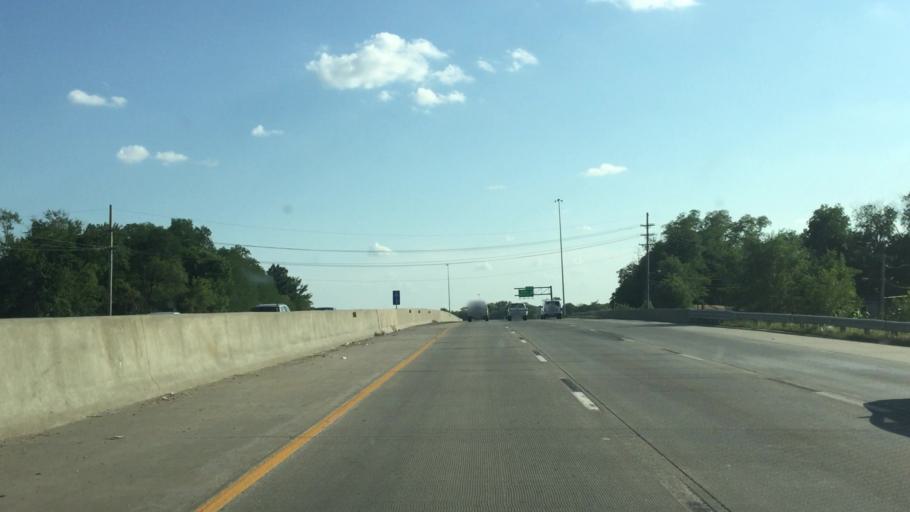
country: US
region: Kansas
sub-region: Wyandotte County
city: Kansas City
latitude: 39.1212
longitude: -94.6790
